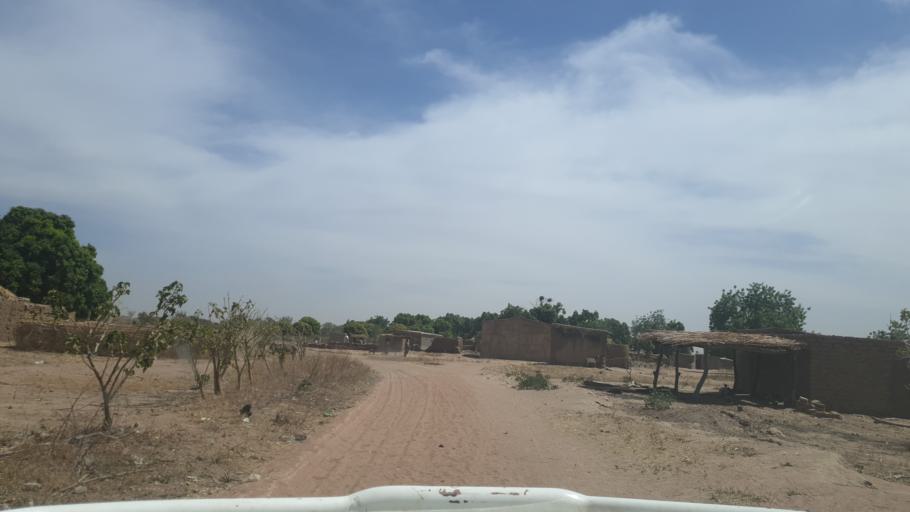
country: ML
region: Sikasso
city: Yorosso
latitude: 12.2821
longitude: -4.6852
